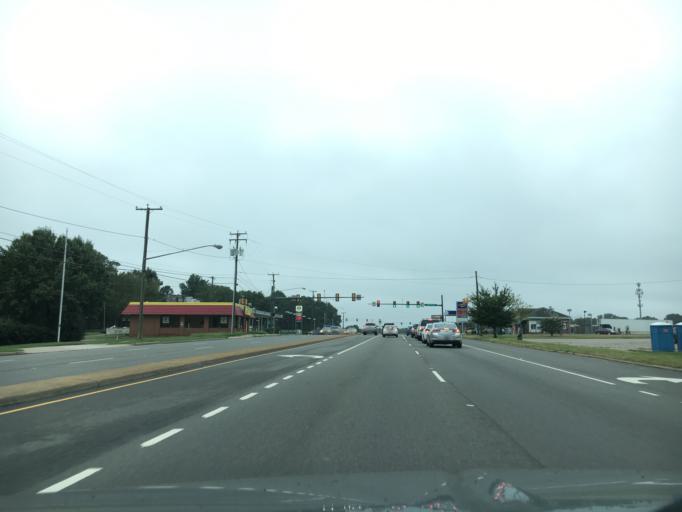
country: US
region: Virginia
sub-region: Chesterfield County
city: Bon Air
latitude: 37.4805
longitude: -77.5093
